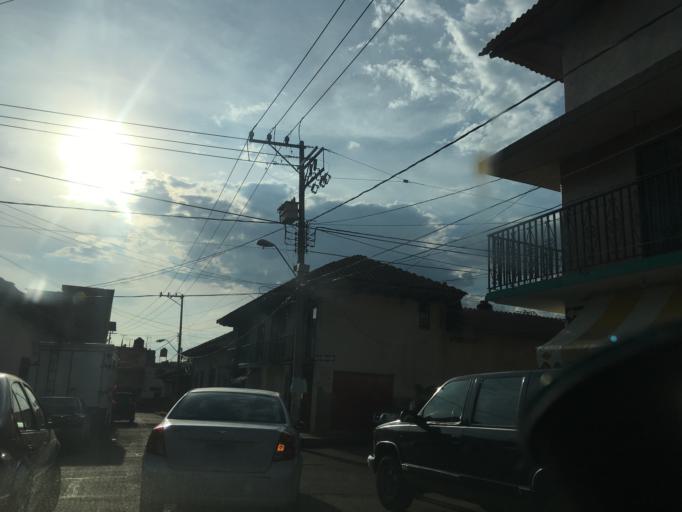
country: MX
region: Michoacan
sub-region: Tingueindin
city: Tingueindin
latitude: 19.7395
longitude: -102.4814
